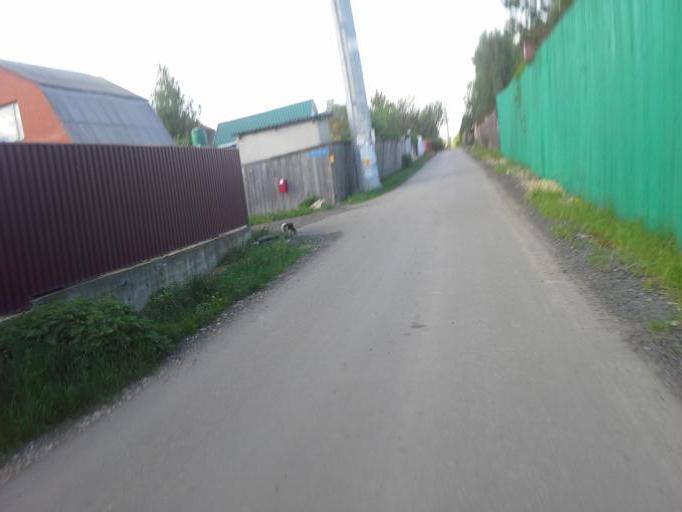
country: RU
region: Moskovskaya
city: Zhavoronki
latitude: 55.6677
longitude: 37.1419
